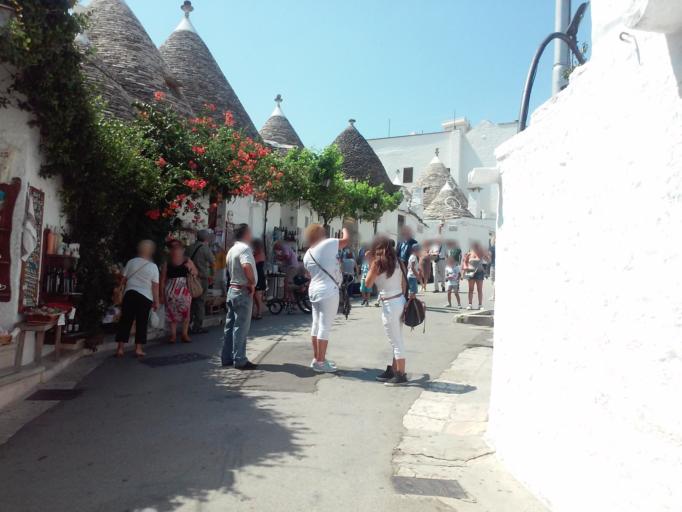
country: IT
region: Apulia
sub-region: Provincia di Bari
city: Alberobello
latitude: 40.7817
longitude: 17.2367
